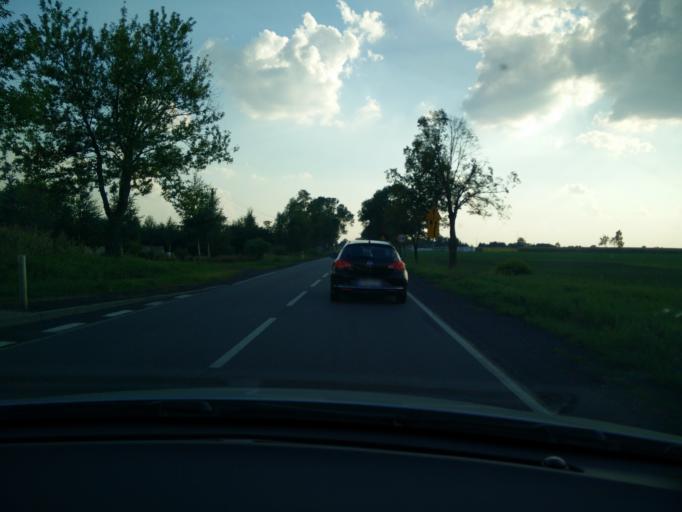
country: PL
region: Greater Poland Voivodeship
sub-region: Powiat wrzesinski
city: Miloslaw
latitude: 52.2518
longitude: 17.5248
